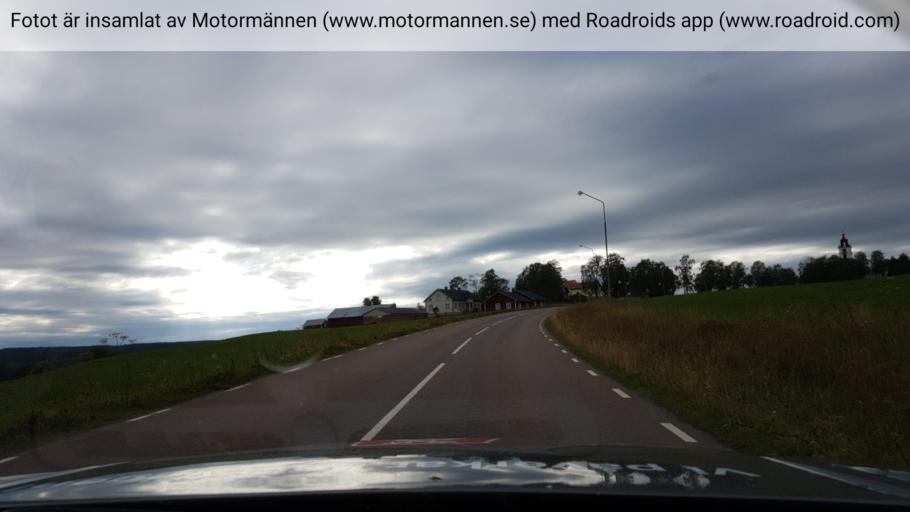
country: SE
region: Jaemtland
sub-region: Krokoms Kommun
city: Valla
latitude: 63.3835
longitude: 13.9467
